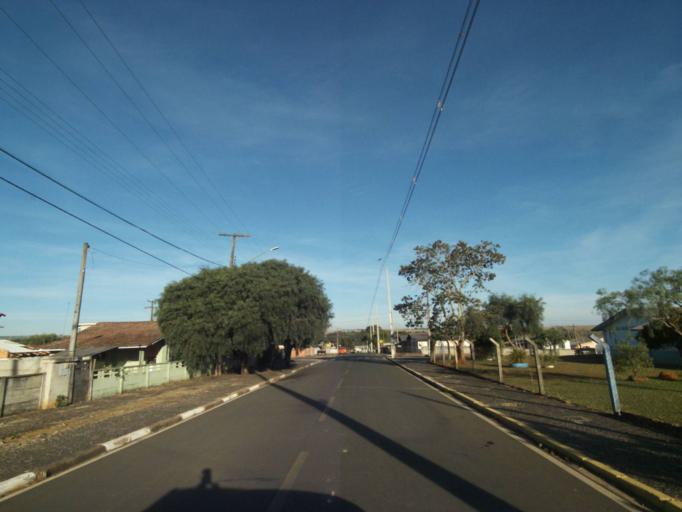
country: BR
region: Parana
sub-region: Tibagi
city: Tibagi
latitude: -24.5245
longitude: -50.4029
